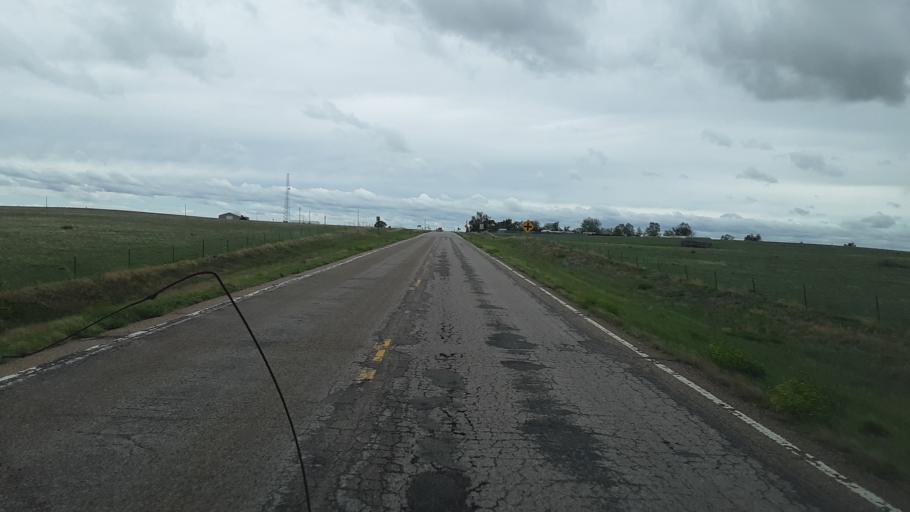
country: US
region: Colorado
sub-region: Lincoln County
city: Hugo
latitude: 38.8519
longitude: -103.6949
